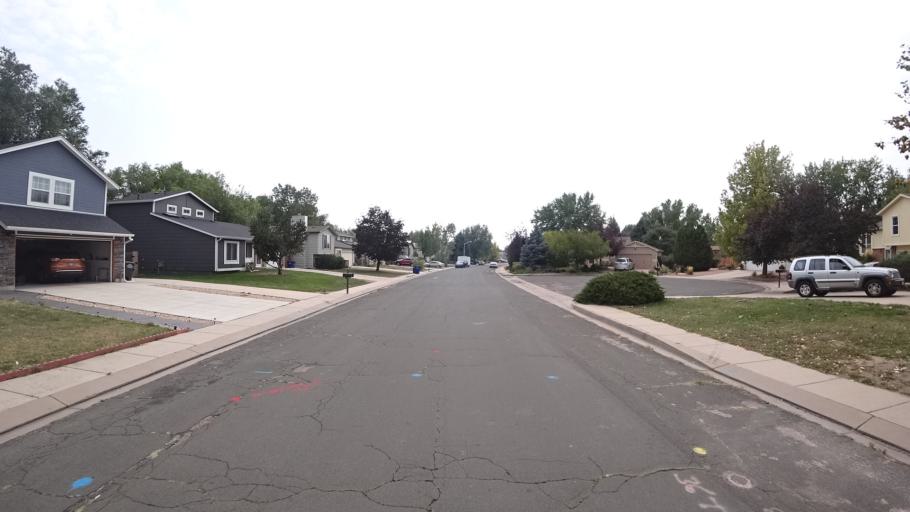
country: US
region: Colorado
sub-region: El Paso County
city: Stratmoor
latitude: 38.8173
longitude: -104.7439
